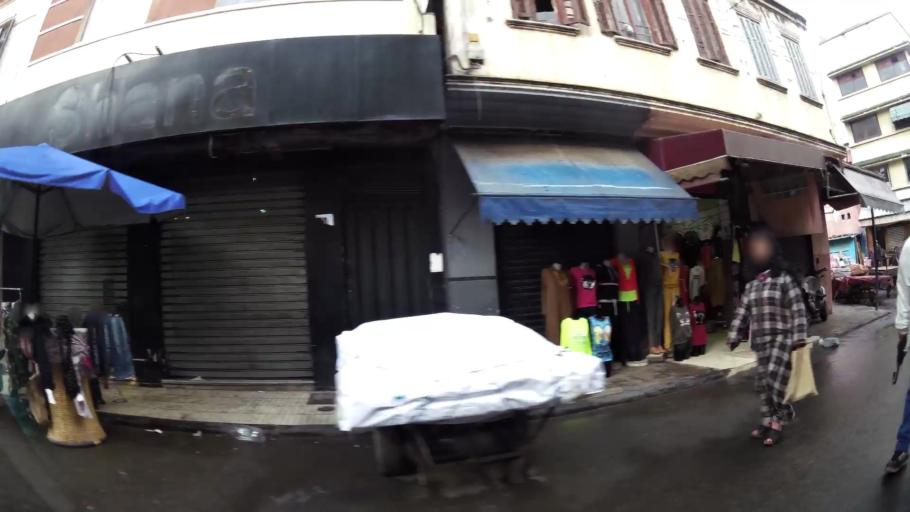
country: MA
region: Grand Casablanca
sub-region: Casablanca
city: Casablanca
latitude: 33.5716
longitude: -7.6025
